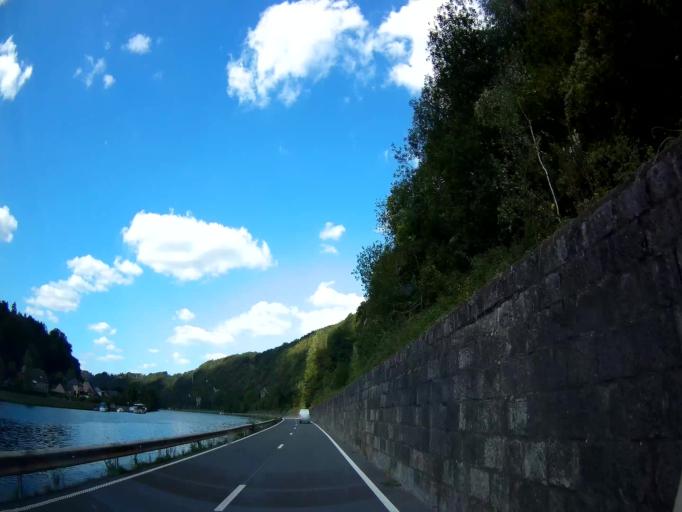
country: BE
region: Wallonia
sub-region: Province de Namur
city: Hastiere-Lavaux
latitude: 50.2103
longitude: 4.8488
